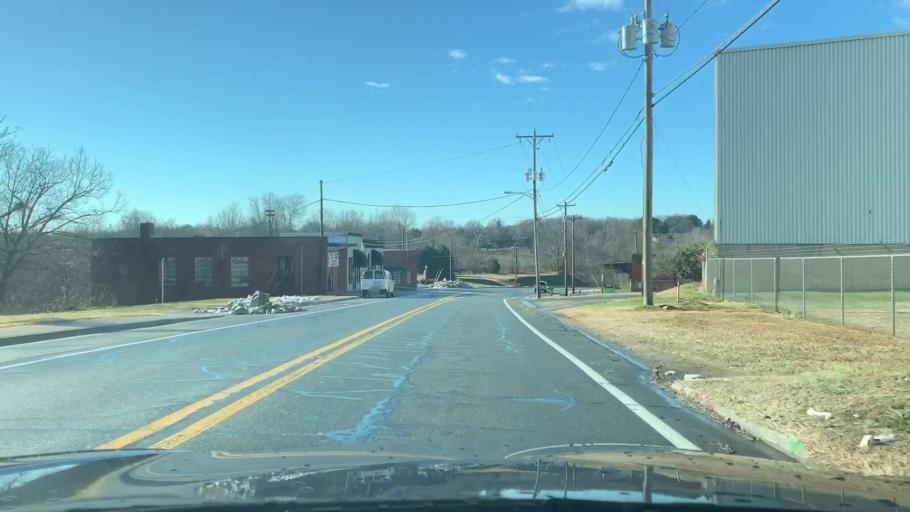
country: US
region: North Carolina
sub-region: Alamance County
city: Haw River
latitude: 36.0906
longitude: -79.3657
